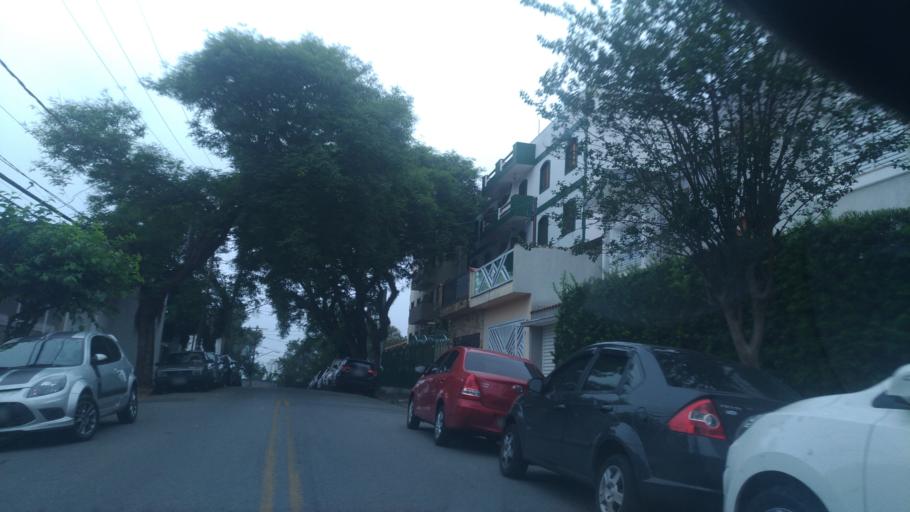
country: BR
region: Sao Paulo
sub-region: Sao Bernardo Do Campo
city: Sao Bernardo do Campo
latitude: -23.6986
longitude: -46.5597
